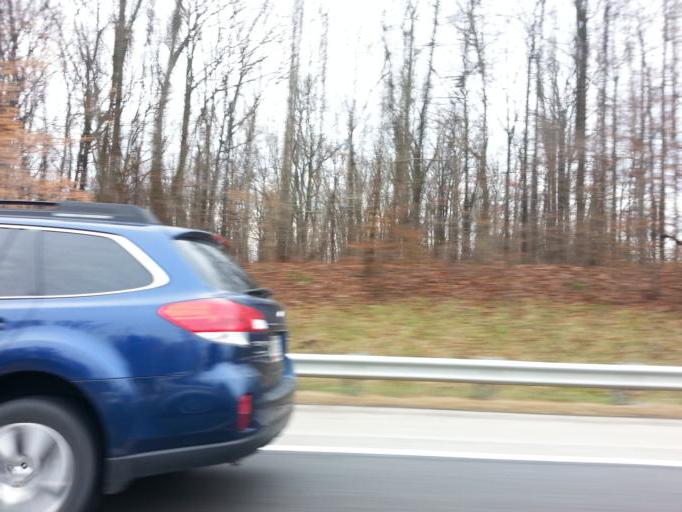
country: US
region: Indiana
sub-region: Ripley County
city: Sunman
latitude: 39.2803
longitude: -85.1088
